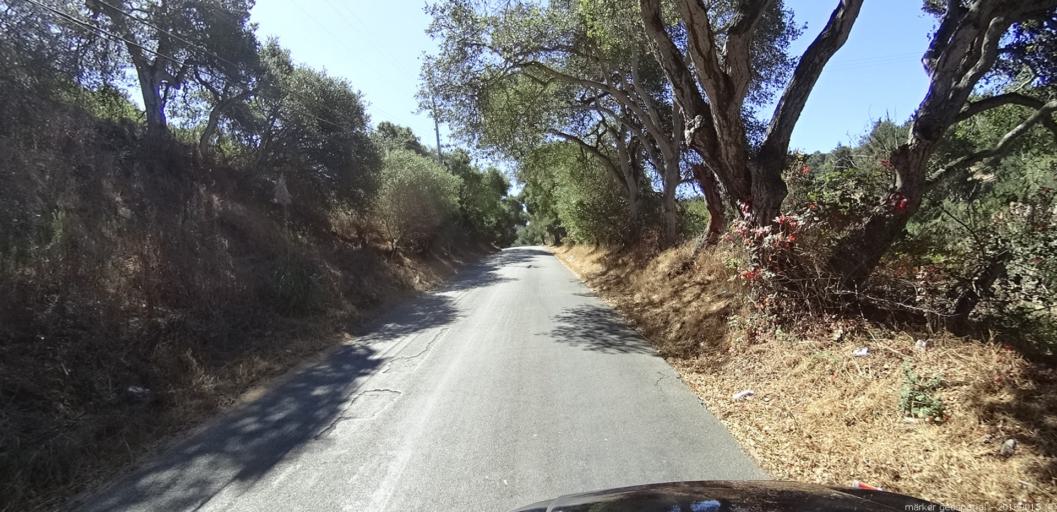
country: US
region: California
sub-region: Monterey County
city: Las Lomas
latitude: 36.8526
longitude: -121.7085
